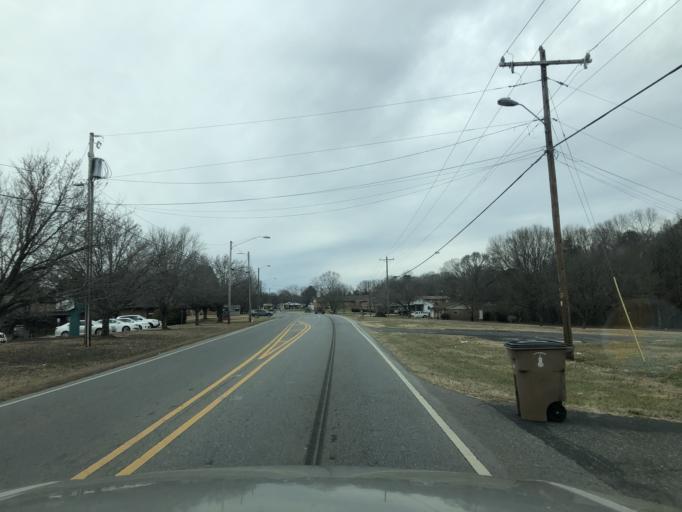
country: US
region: North Carolina
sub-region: Cleveland County
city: Shelby
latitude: 35.2699
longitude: -81.4803
